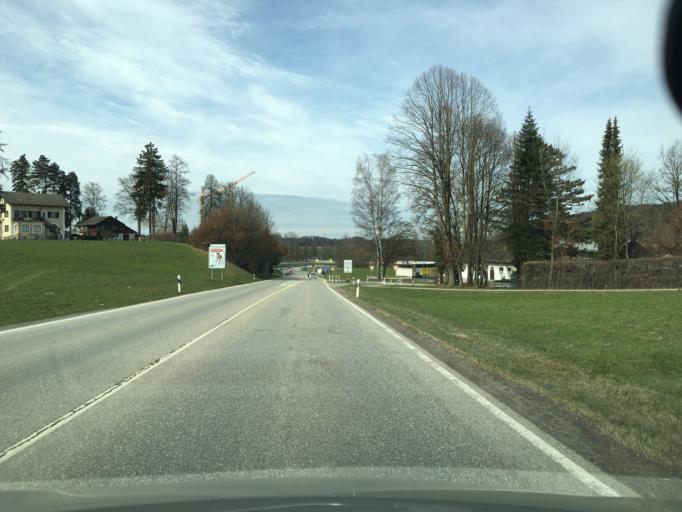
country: DE
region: Bavaria
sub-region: Upper Bavaria
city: Siegsdorf
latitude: 47.8236
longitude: 12.6511
